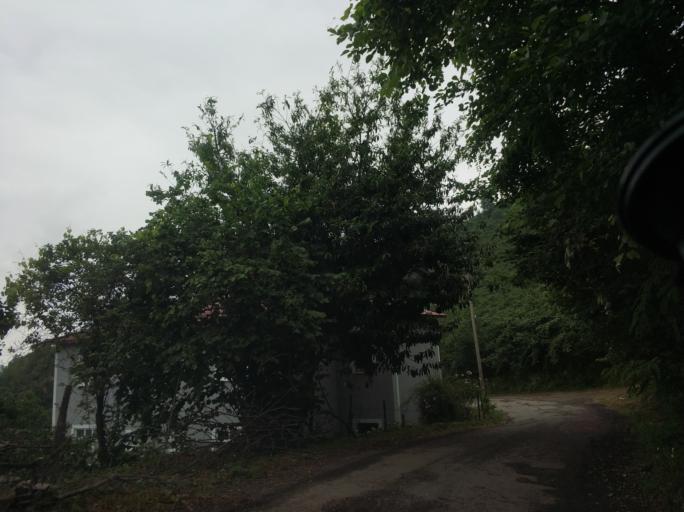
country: TR
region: Giresun
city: Nefsipiraziz
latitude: 40.8942
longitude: 38.0882
